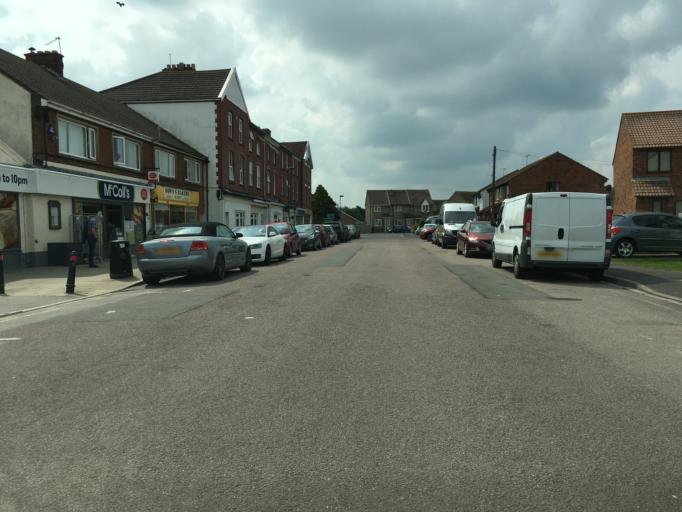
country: GB
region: England
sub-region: South Gloucestershire
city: Severn Beach
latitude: 51.5617
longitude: -2.6659
